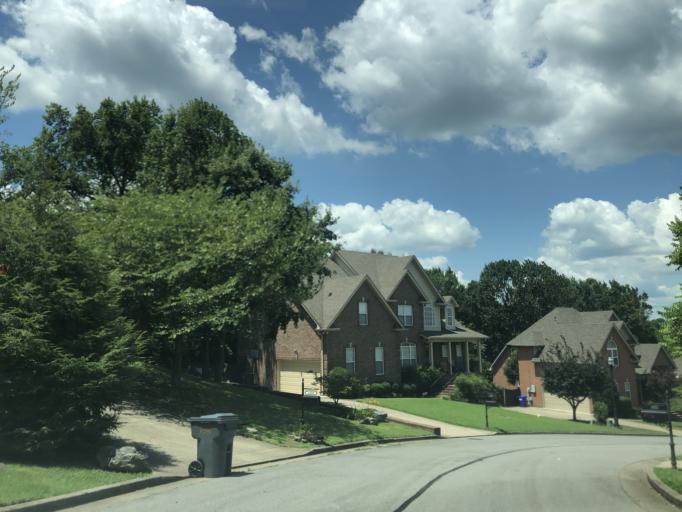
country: US
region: Tennessee
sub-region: Wilson County
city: Green Hill
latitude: 36.1976
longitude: -86.5919
